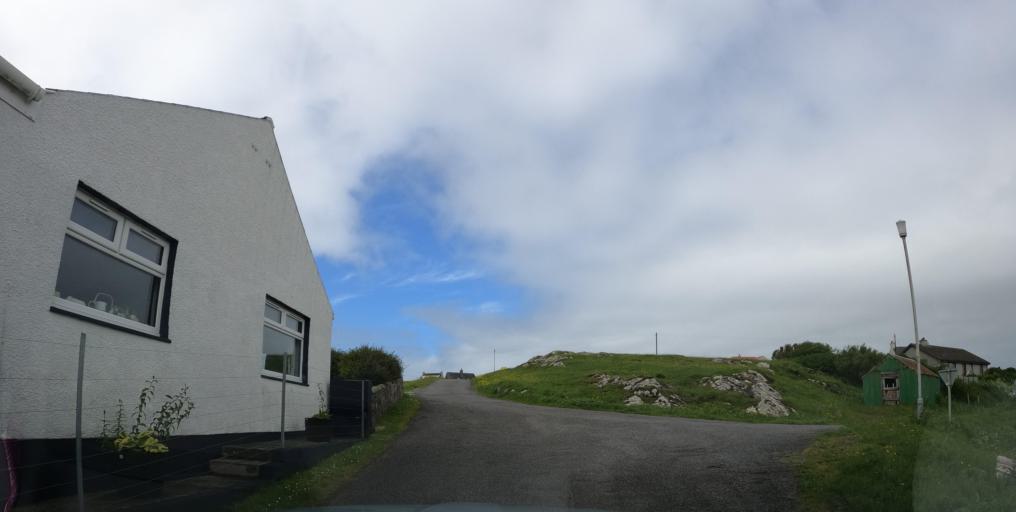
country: GB
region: Scotland
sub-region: Eilean Siar
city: Isle of South Uist
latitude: 57.0859
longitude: -7.3011
